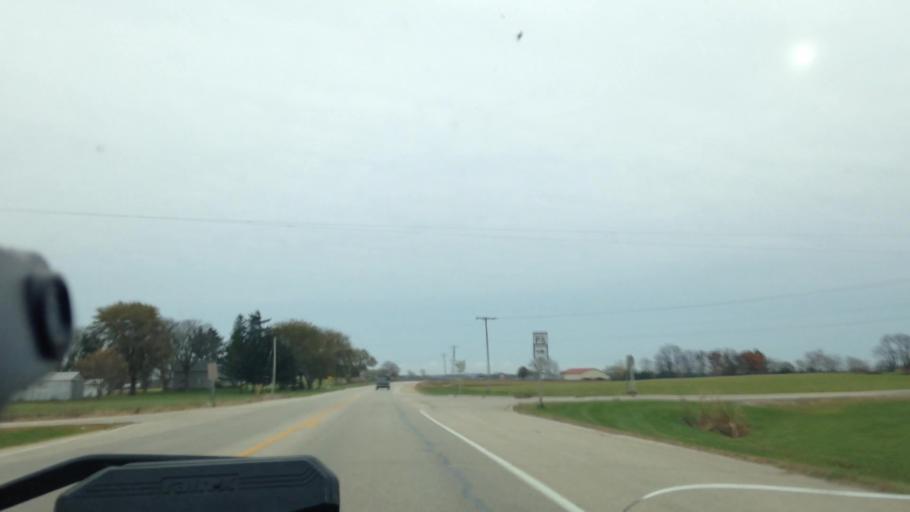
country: US
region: Wisconsin
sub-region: Dodge County
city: Theresa
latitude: 43.4249
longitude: -88.4211
